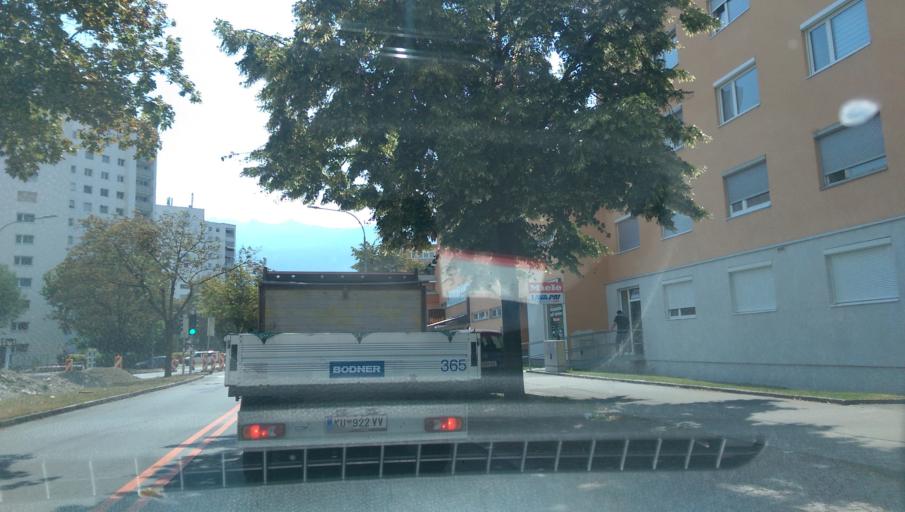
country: AT
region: Tyrol
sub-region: Innsbruck Stadt
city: Innsbruck
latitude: 47.2692
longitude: 11.4199
